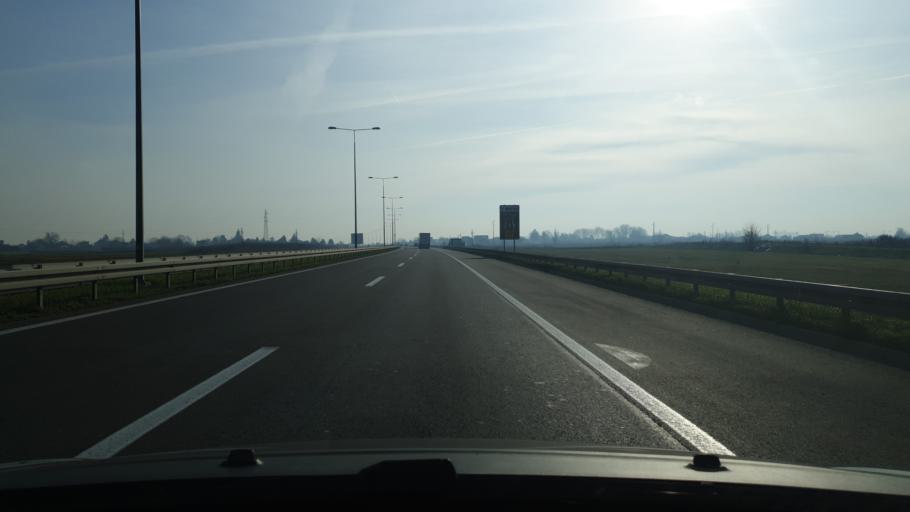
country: RS
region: Central Serbia
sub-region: Belgrade
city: Surcin
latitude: 44.7983
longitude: 20.2549
